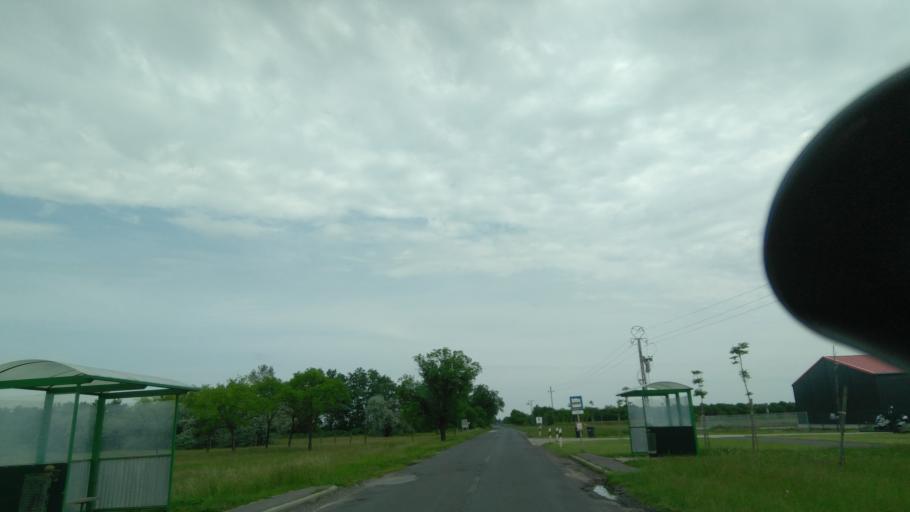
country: HU
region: Bekes
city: Szeghalom
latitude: 47.0355
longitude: 21.1816
